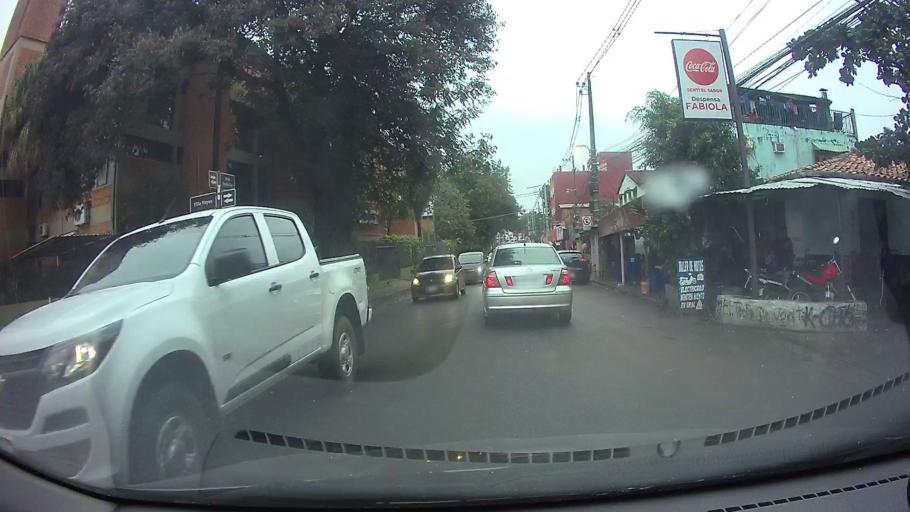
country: PY
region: Central
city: Villa Elisa
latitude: -25.3422
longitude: -57.5664
